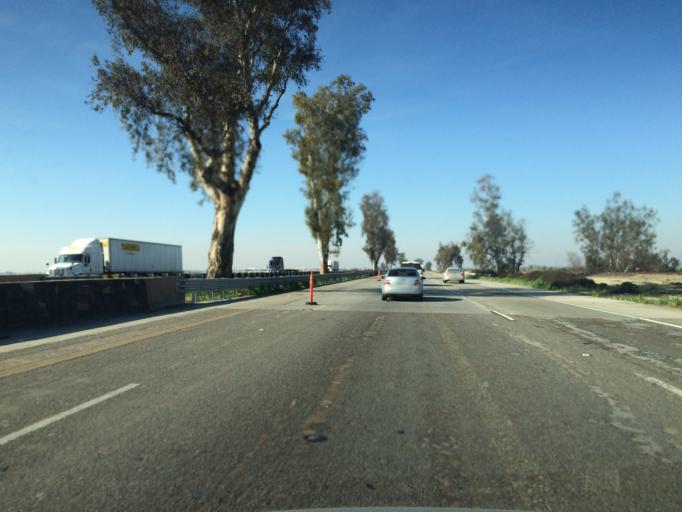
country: US
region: California
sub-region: Tulare County
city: Goshen
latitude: 36.4033
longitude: -119.4555
